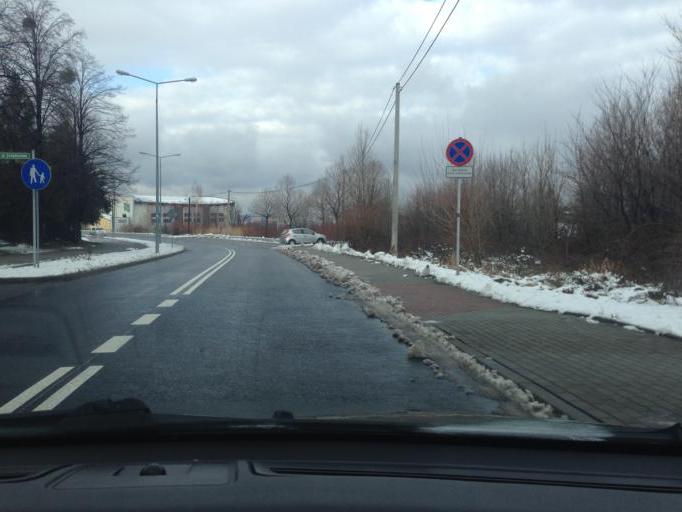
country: PL
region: Silesian Voivodeship
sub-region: Powiat bielski
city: Bystra
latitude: 49.7822
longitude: 19.0232
